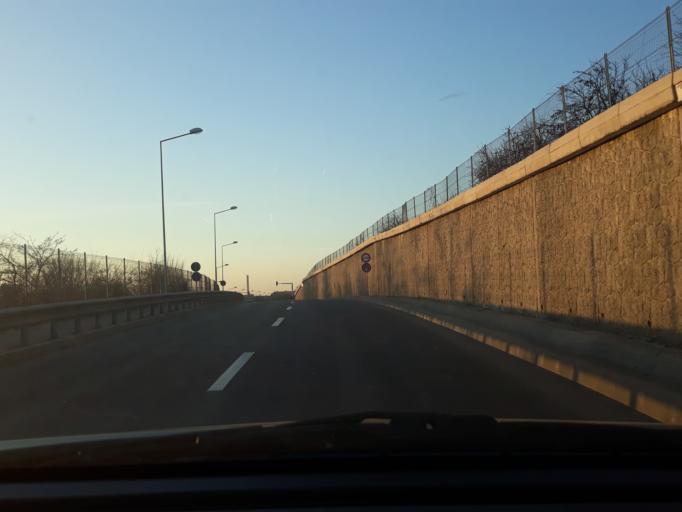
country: RO
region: Bihor
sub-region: Comuna Biharea
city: Oradea
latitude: 47.0602
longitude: 21.9457
